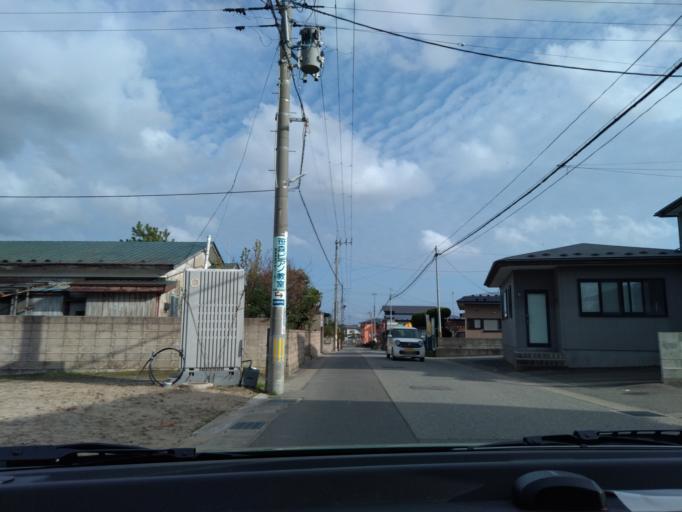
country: JP
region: Akita
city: Akita Shi
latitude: 39.7707
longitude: 140.0822
